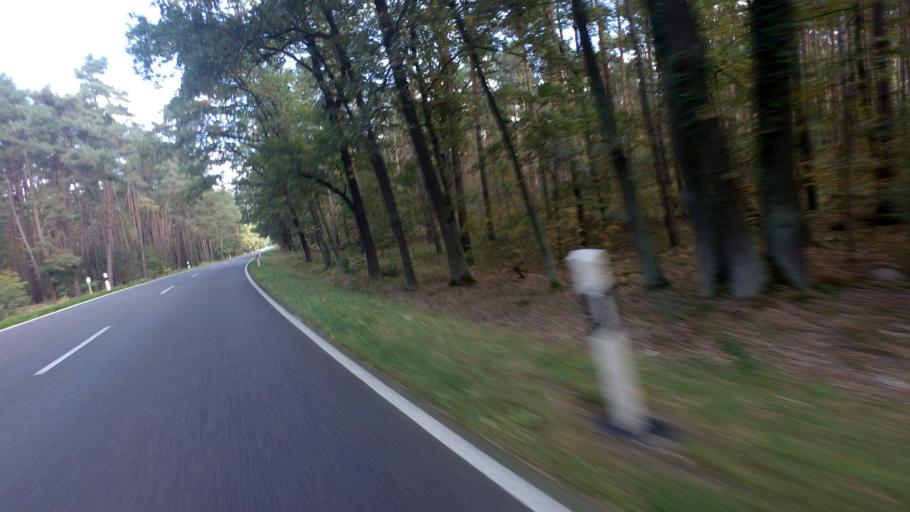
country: DE
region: Saxony-Anhalt
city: Holzdorf
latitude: 51.8412
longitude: 13.1433
